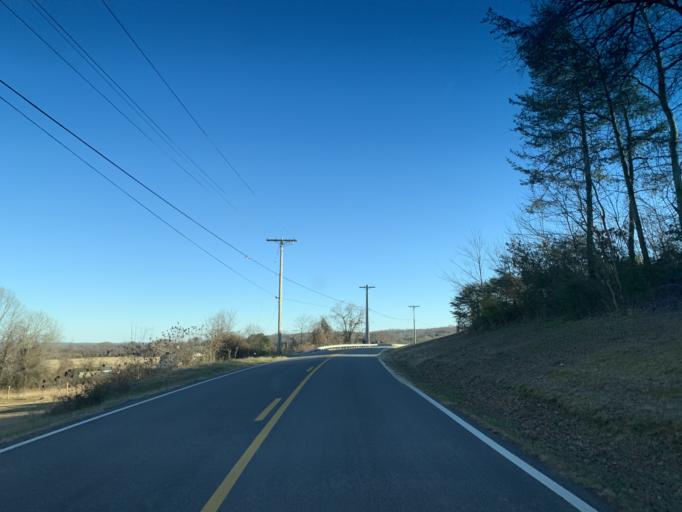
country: US
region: Maryland
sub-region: Saint Mary's County
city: Golden Beach
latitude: 38.4568
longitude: -76.6821
